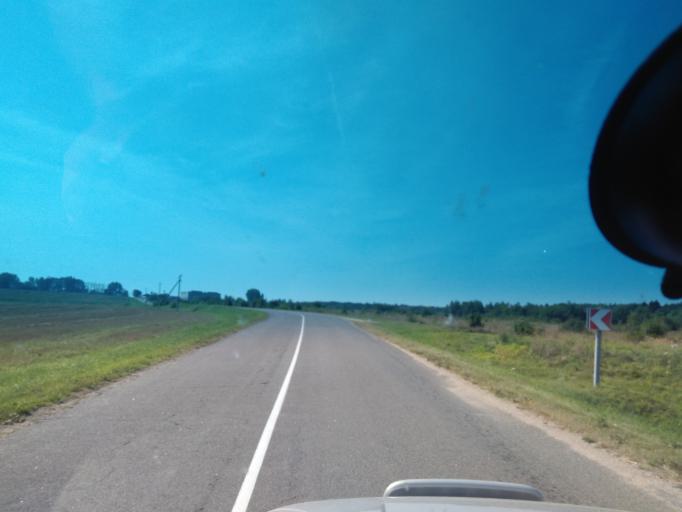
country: BY
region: Minsk
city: Kapyl'
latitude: 53.2158
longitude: 27.1288
